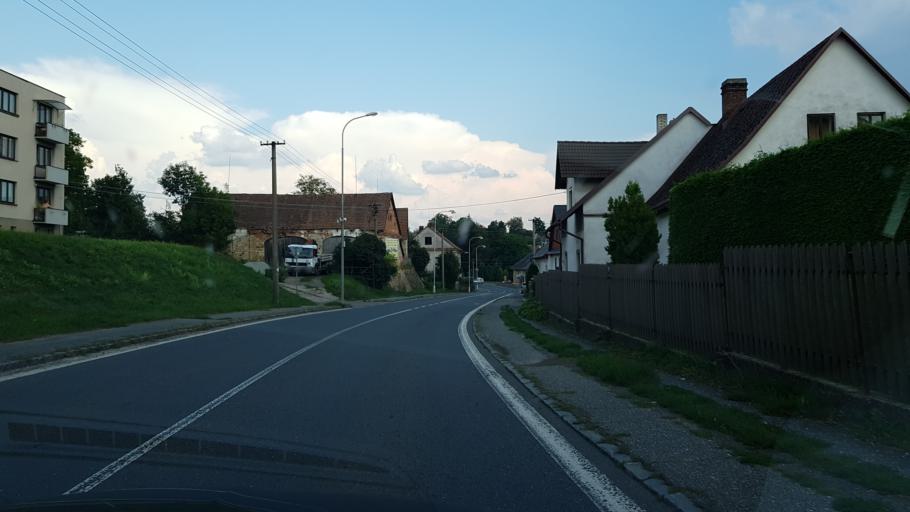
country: CZ
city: Doudleby nad Orlici
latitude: 50.1105
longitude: 16.2579
